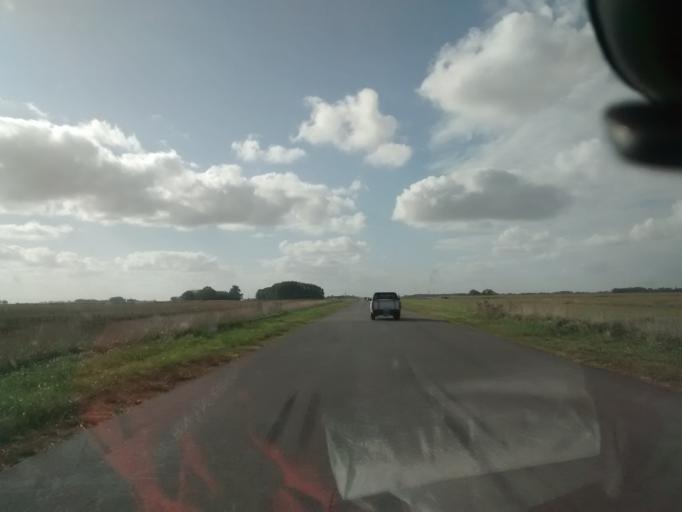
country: AR
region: Buenos Aires
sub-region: Partido de Ayacucho
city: Ayacucho
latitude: -37.2073
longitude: -58.5039
